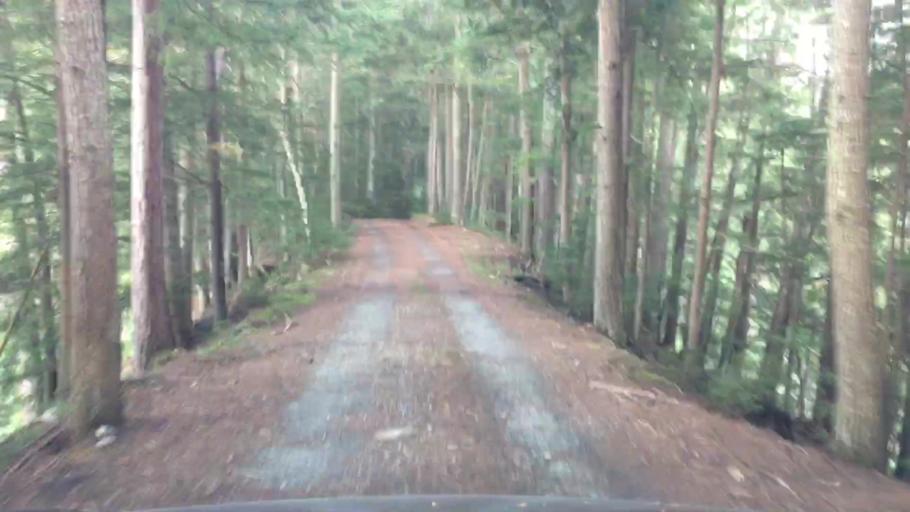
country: US
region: New Hampshire
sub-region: Grafton County
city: Littleton
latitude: 44.3050
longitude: -71.8902
